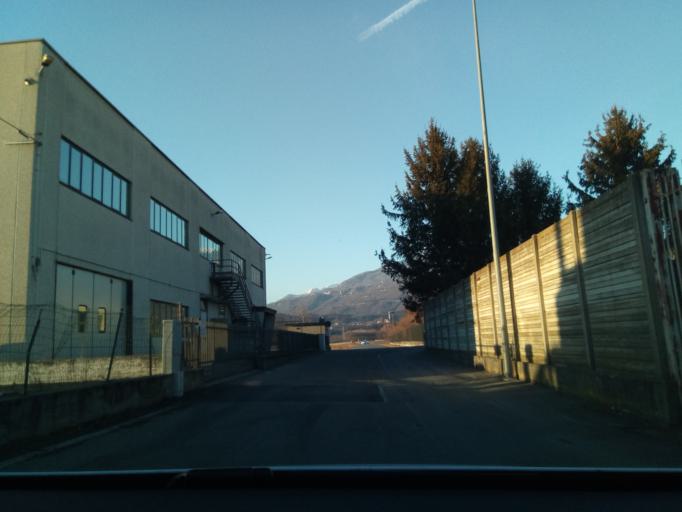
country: IT
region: Piedmont
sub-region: Provincia di Torino
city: Cascinette d'Ivrea
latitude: 45.4728
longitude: 7.9173
